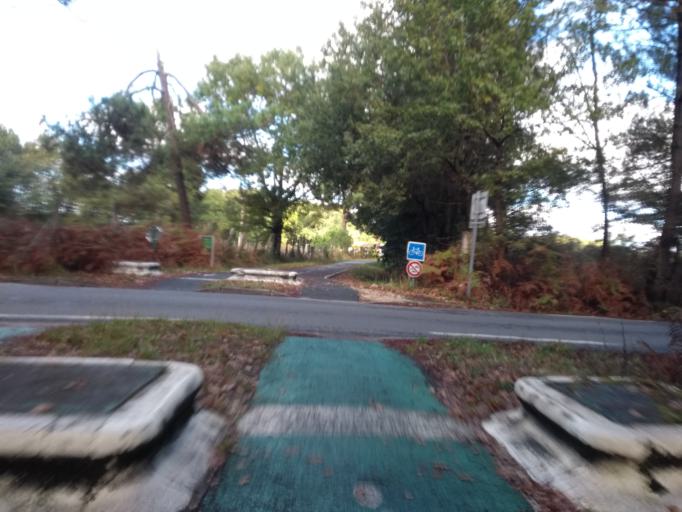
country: FR
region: Aquitaine
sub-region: Departement de la Gironde
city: Saint-Aubin-de-Medoc
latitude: 44.8008
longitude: -0.7082
